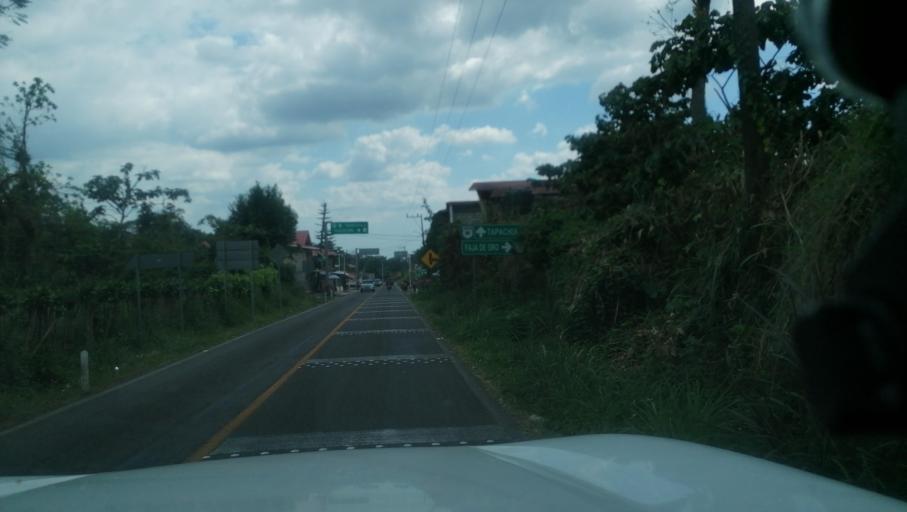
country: MX
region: Chiapas
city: Cacahoatan
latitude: 15.0322
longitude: -92.1536
